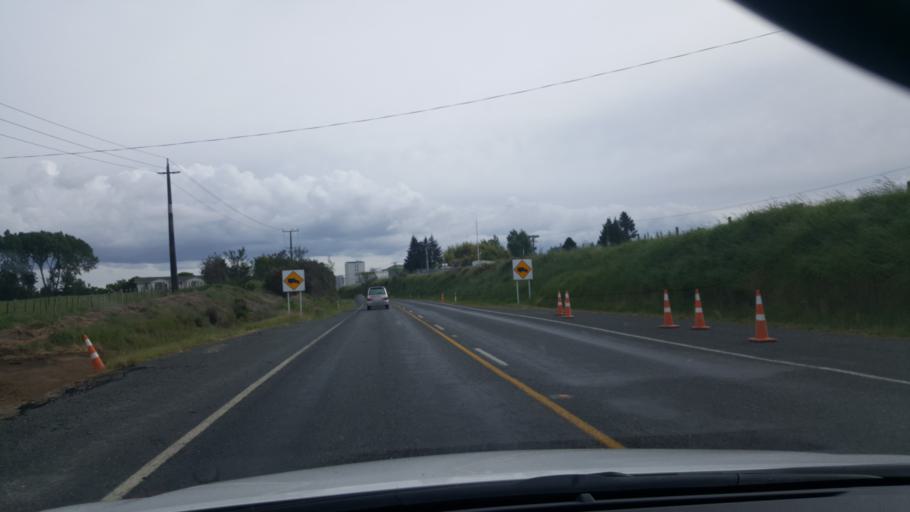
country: NZ
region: Bay of Plenty
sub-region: Rotorua District
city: Rotorua
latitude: -38.4207
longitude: 176.3181
